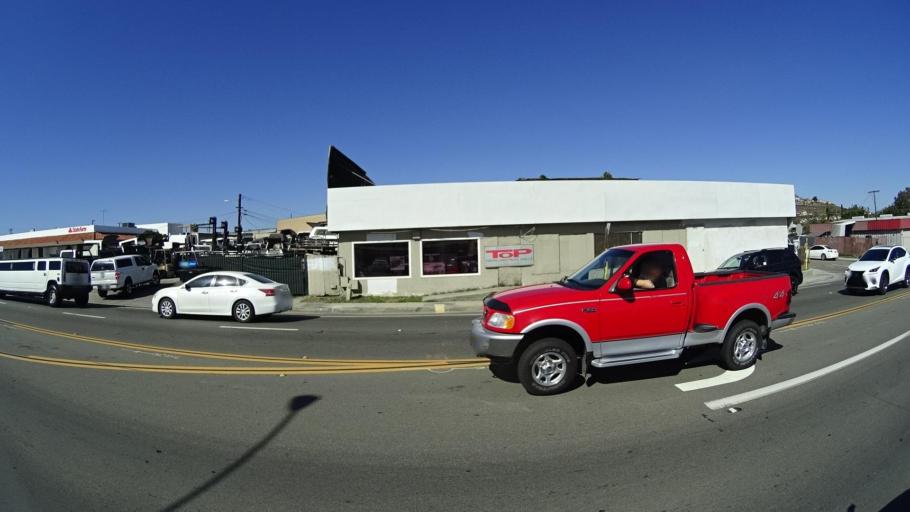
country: US
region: California
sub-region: San Diego County
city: La Presa
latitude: 32.7078
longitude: -116.9966
